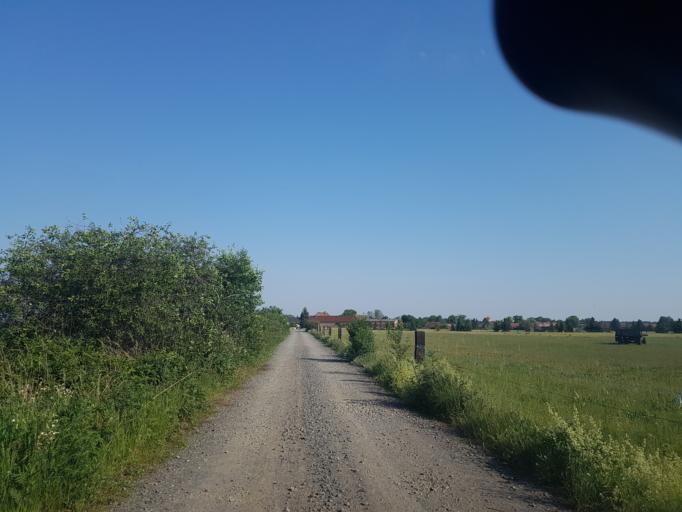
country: DE
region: Brandenburg
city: Finsterwalde
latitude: 51.5624
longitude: 13.6700
